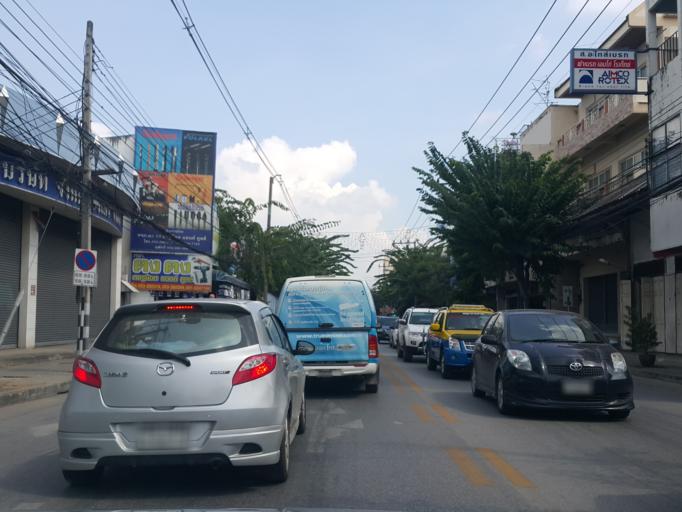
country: TH
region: Chiang Mai
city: Chiang Mai
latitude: 18.7872
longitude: 99.0076
